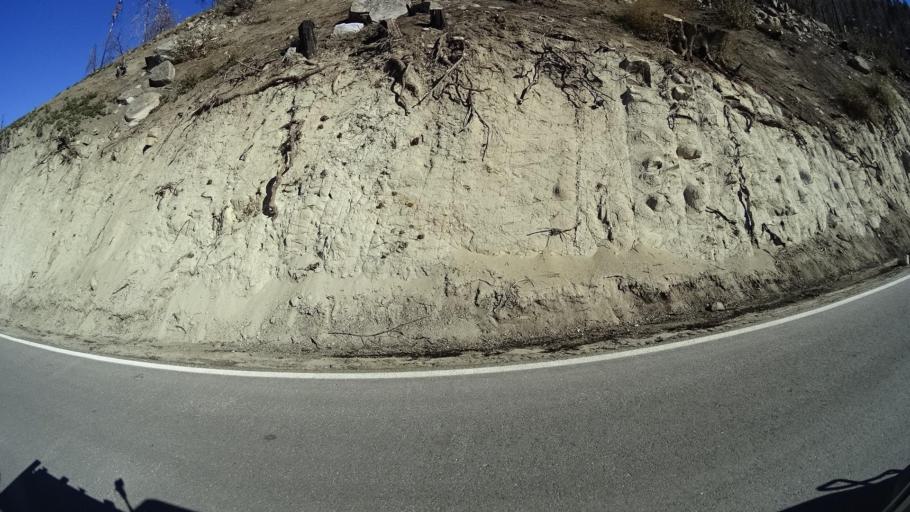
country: US
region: California
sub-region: Kern County
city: Alta Sierra
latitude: 35.7479
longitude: -118.5577
